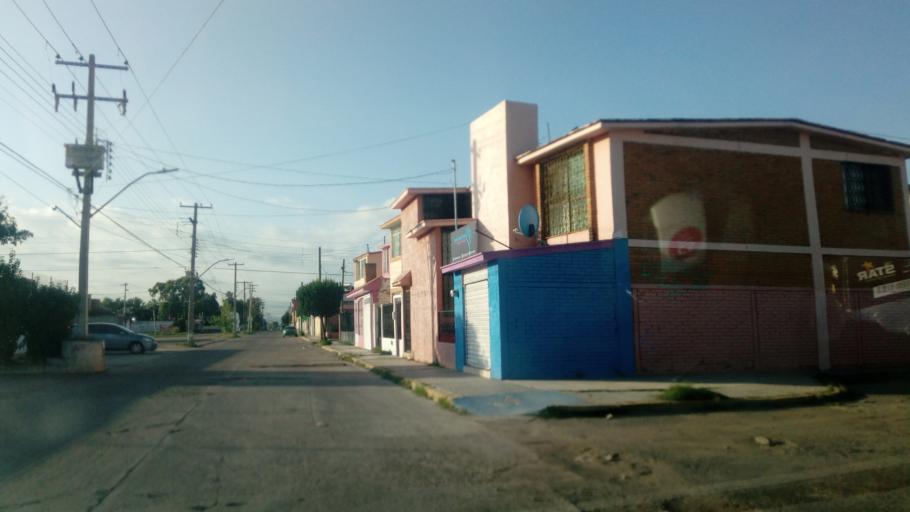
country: MX
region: Durango
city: Victoria de Durango
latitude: 24.0504
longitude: -104.6181
